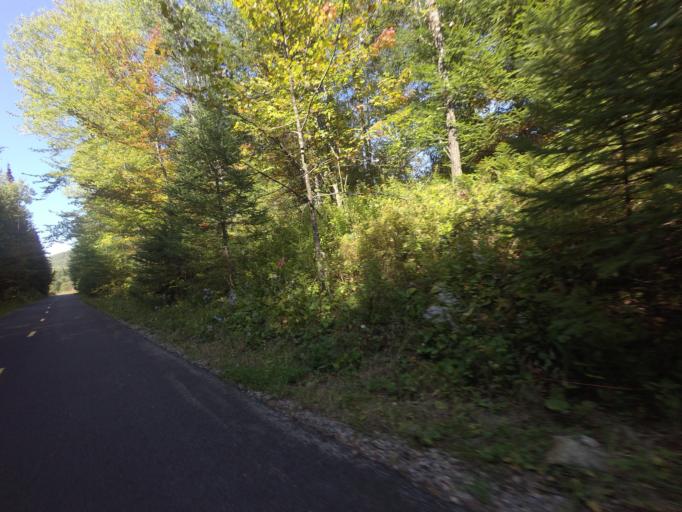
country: CA
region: Quebec
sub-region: Laurentides
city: Mont-Tremblant
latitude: 46.1281
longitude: -74.5492
